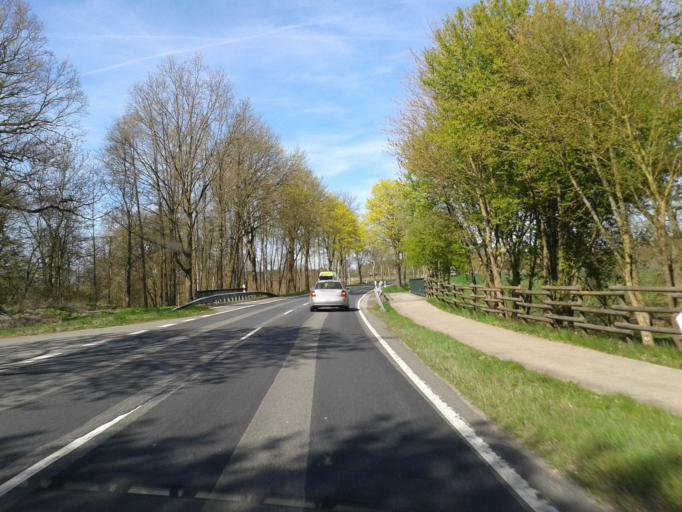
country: DE
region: Lower Saxony
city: Gerdau
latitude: 52.9660
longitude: 10.4008
